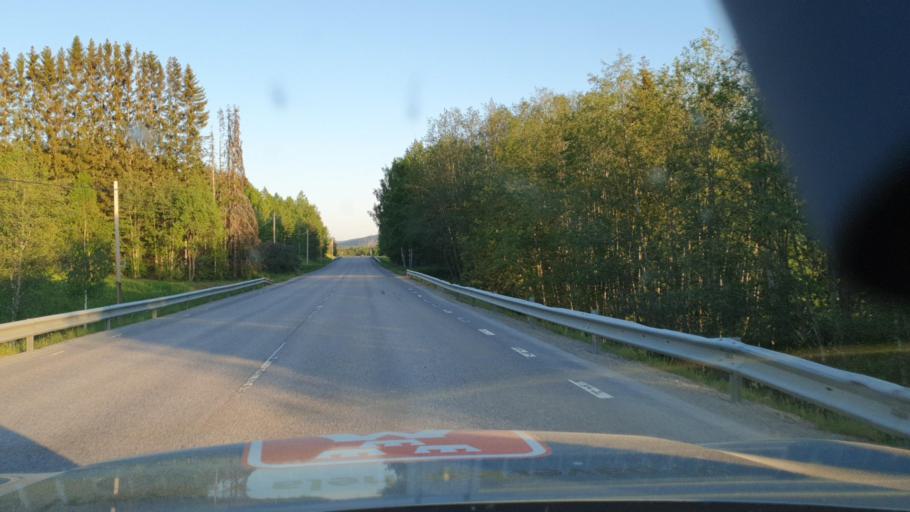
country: SE
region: Vaesternorrland
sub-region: Solleftea Kommun
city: Solleftea
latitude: 63.1898
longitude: 17.2436
